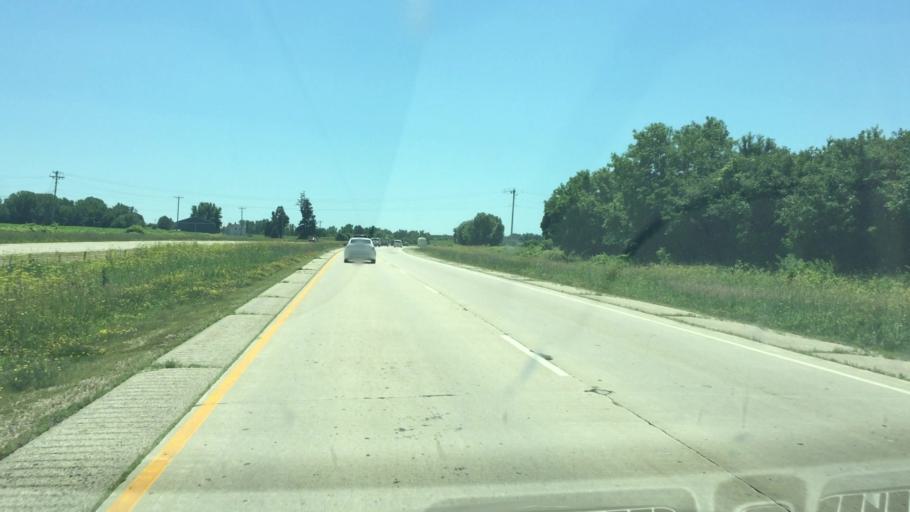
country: US
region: Wisconsin
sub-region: Dane County
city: Sun Prairie
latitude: 43.2179
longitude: -89.1649
